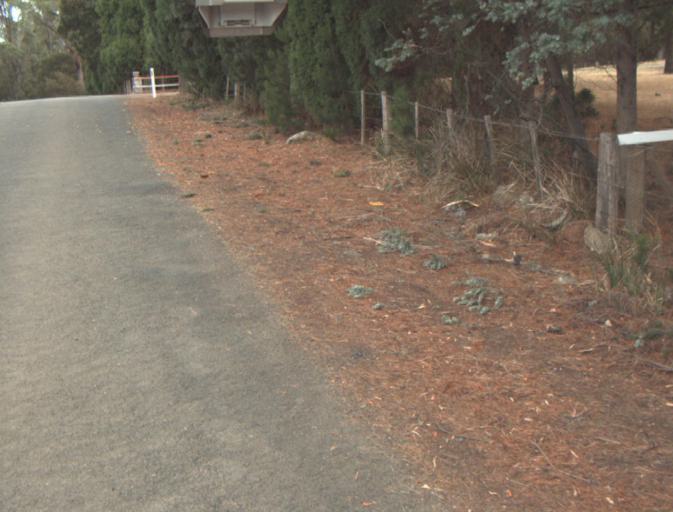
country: AU
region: Tasmania
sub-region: Launceston
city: Mayfield
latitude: -41.2815
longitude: 147.0421
